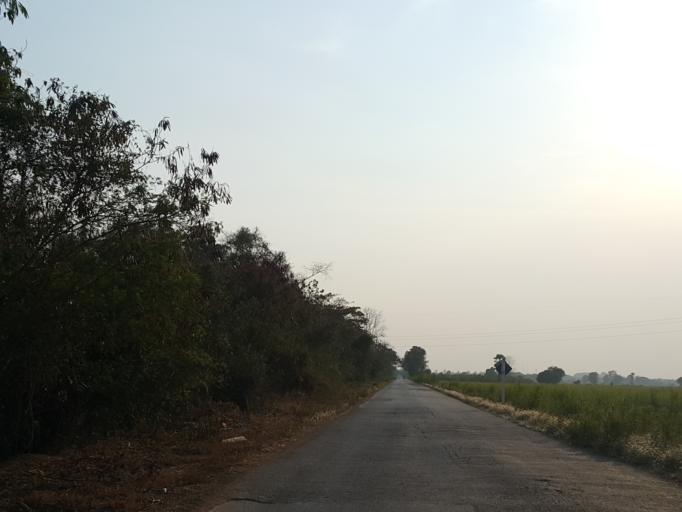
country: TH
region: Sukhothai
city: Si Samrong
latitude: 17.2209
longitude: 99.9268
